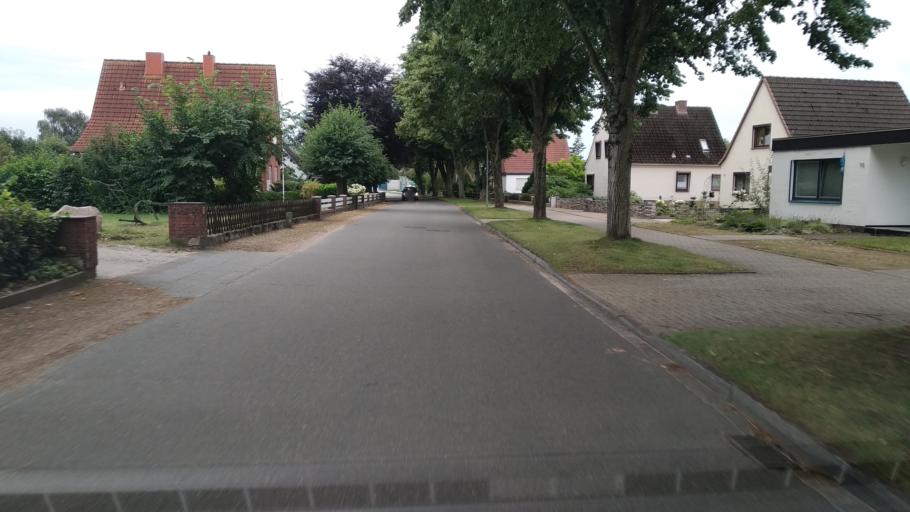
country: DE
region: Schleswig-Holstein
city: Schuby
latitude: 54.5226
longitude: 9.4815
